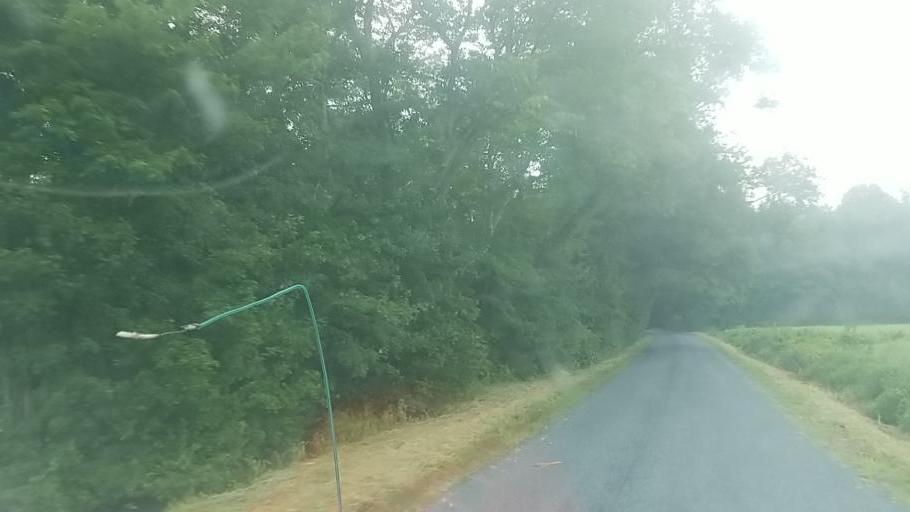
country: US
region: Maryland
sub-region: Wicomico County
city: Pittsville
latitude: 38.4431
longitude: -75.3419
